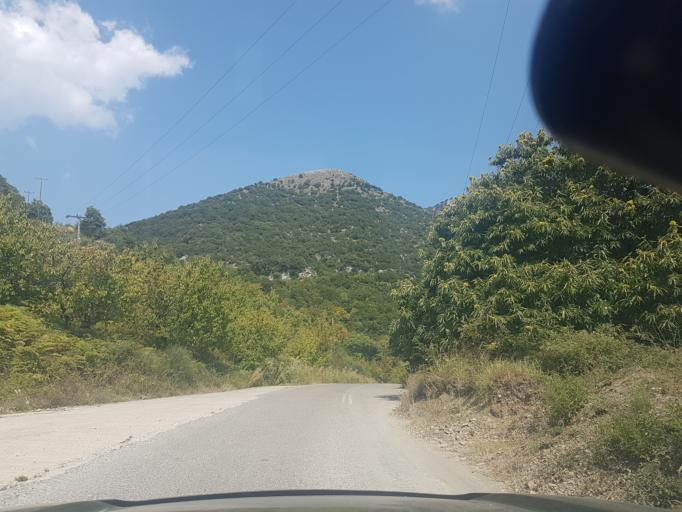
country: GR
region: Central Greece
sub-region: Nomos Evvoias
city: Kymi
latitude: 38.6451
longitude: 23.8999
